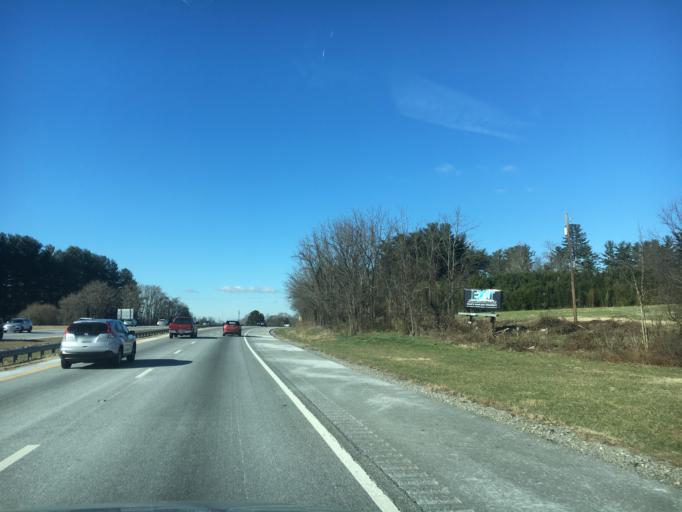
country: US
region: North Carolina
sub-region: Henderson County
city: East Flat Rock
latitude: 35.3053
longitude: -82.4141
